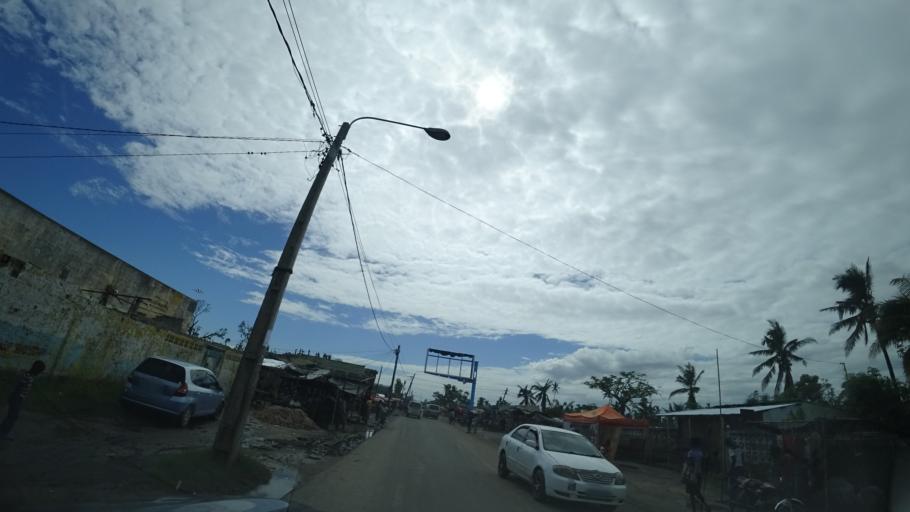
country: MZ
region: Sofala
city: Beira
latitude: -19.7906
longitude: 34.8868
